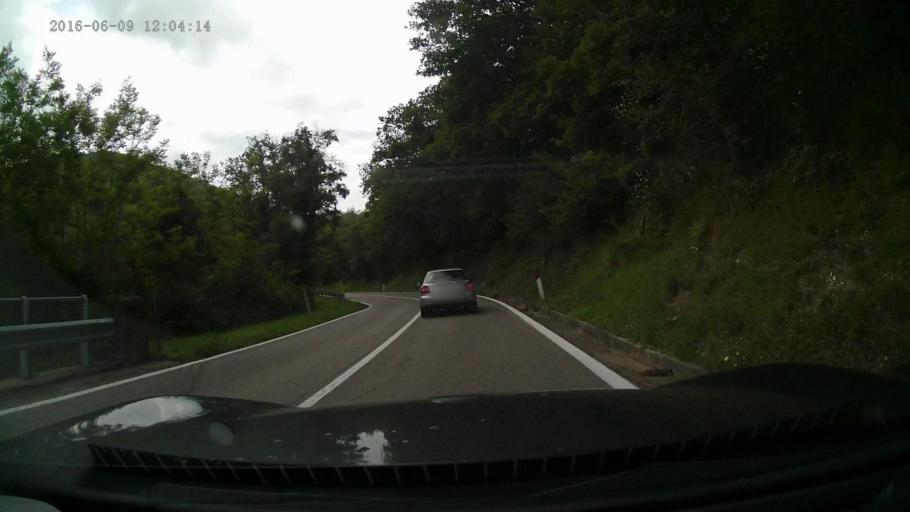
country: IT
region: Tuscany
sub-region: Province of Florence
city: Panzano in Chianti
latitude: 43.5222
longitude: 11.2983
